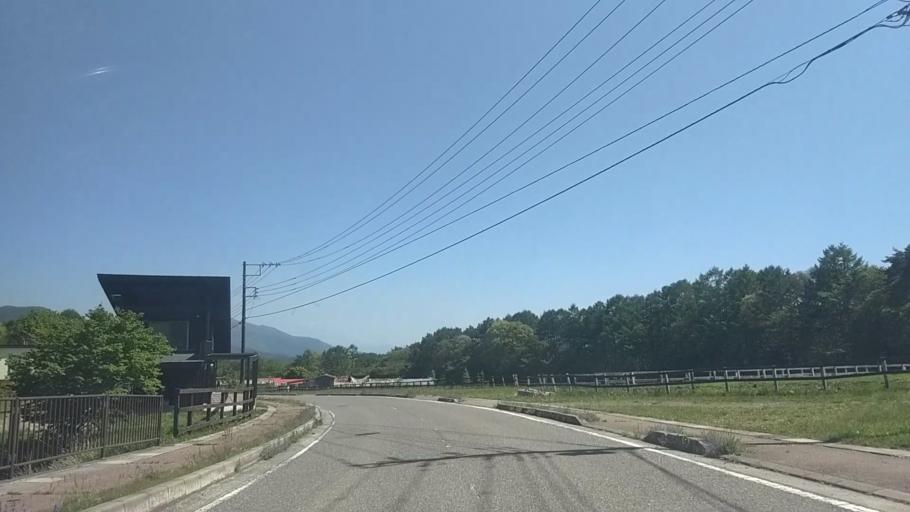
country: JP
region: Yamanashi
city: Nirasaki
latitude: 35.9079
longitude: 138.4321
